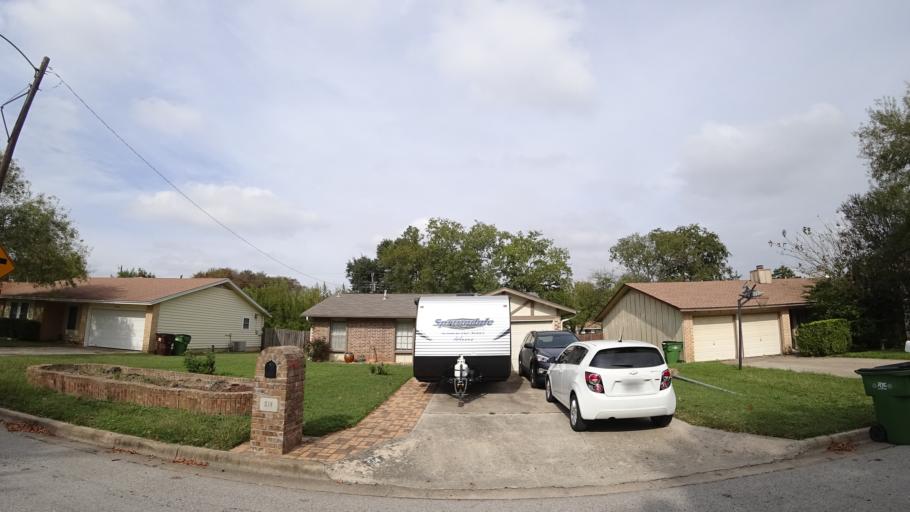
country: US
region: Texas
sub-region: Williamson County
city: Round Rock
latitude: 30.4928
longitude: -97.6840
